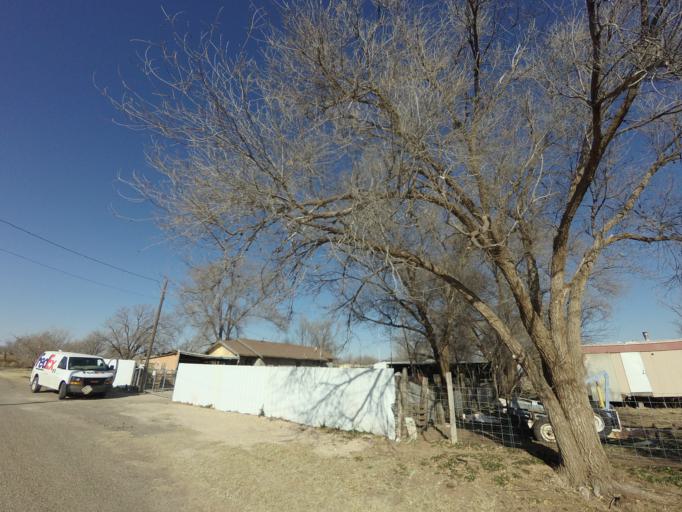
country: US
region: New Mexico
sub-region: Curry County
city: Clovis
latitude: 34.3855
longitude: -103.1841
